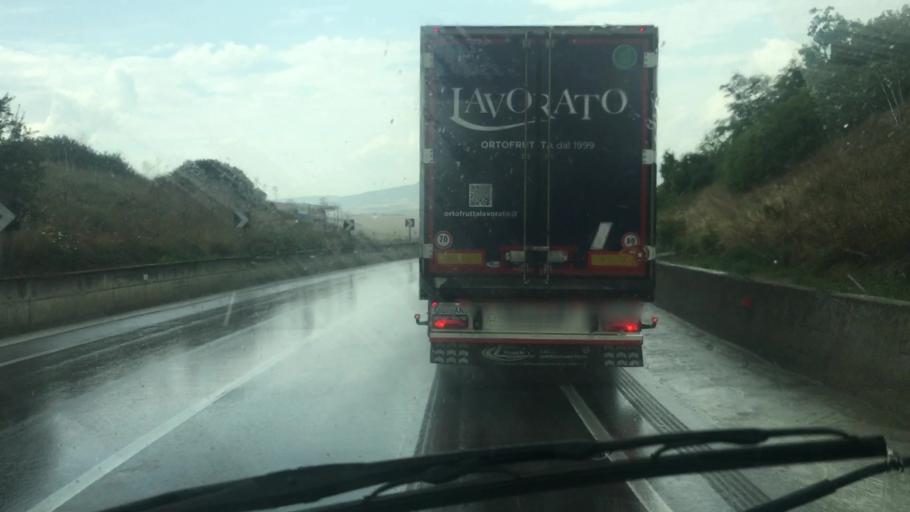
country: IT
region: Basilicate
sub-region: Provincia di Matera
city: Matera
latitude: 40.6299
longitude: 16.5921
